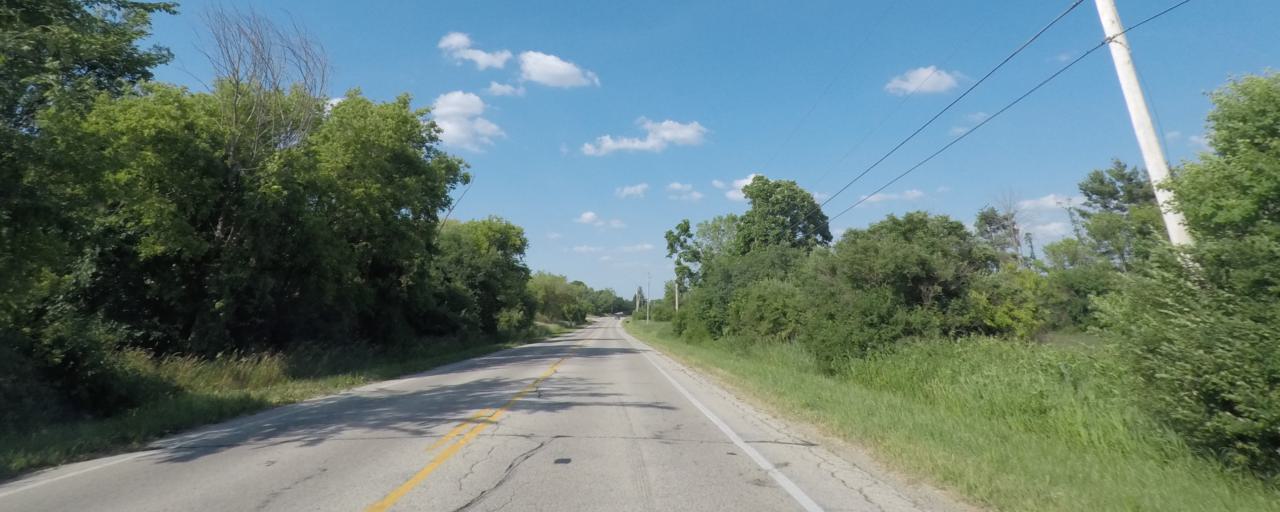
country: US
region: Wisconsin
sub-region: Racine County
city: Tichigan
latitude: 42.8438
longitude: -88.2652
